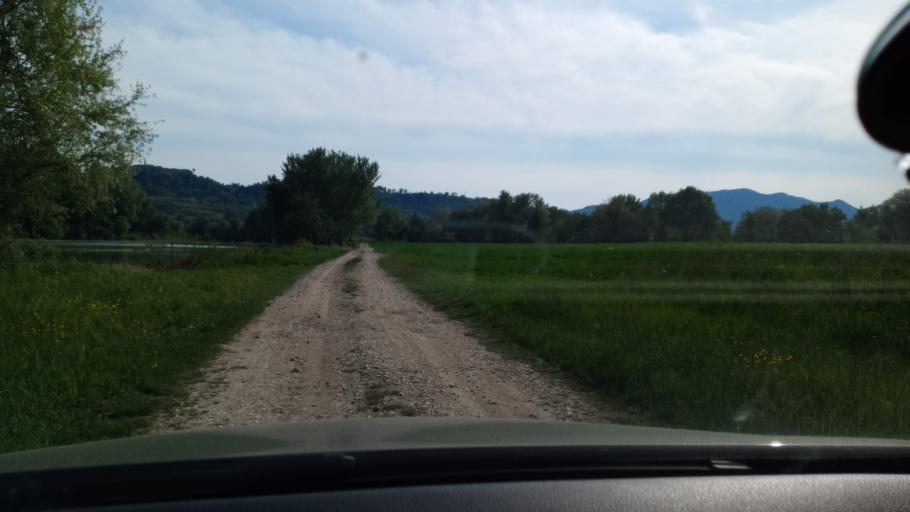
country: IT
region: Latium
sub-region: Citta metropolitana di Roma Capitale
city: Ponzano Romano
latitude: 42.2760
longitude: 12.5789
